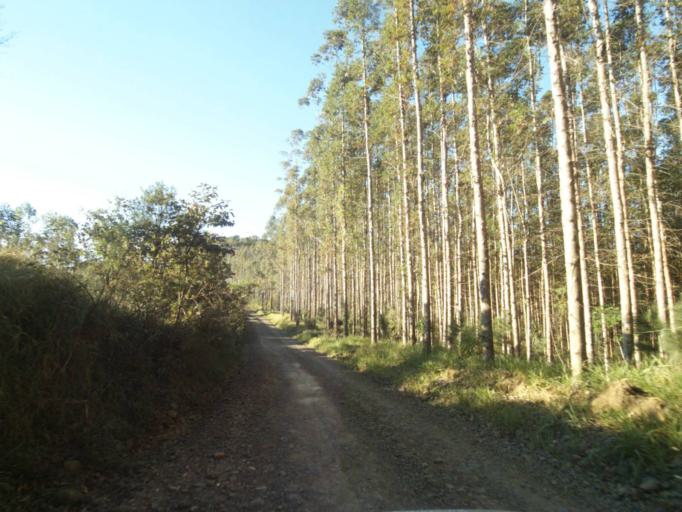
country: BR
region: Parana
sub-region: Telemaco Borba
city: Telemaco Borba
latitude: -24.4911
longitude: -50.5947
